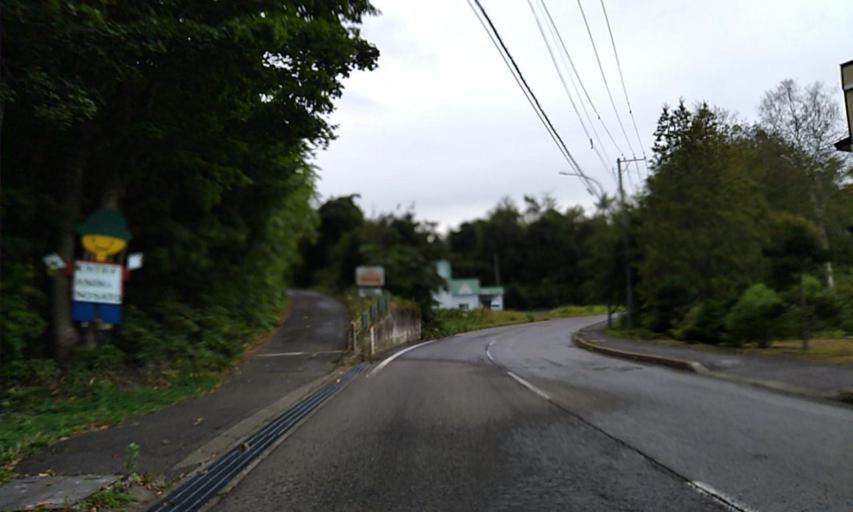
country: JP
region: Hokkaido
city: Abashiri
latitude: 44.0026
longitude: 144.2311
